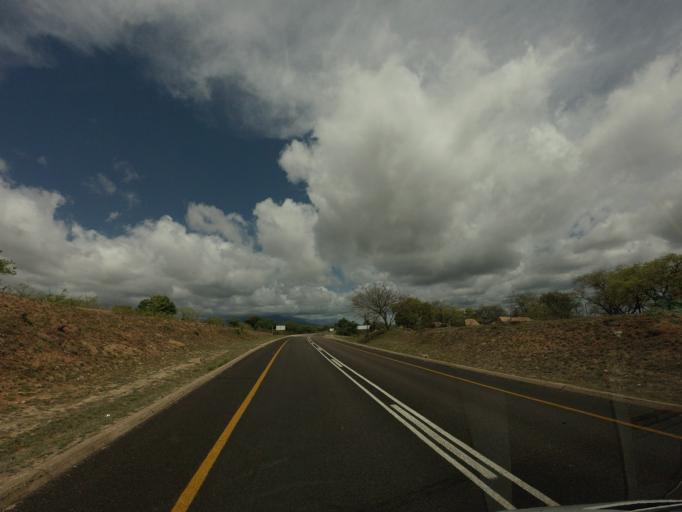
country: ZA
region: Limpopo
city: Thulamahashi
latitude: -24.5672
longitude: 31.0585
